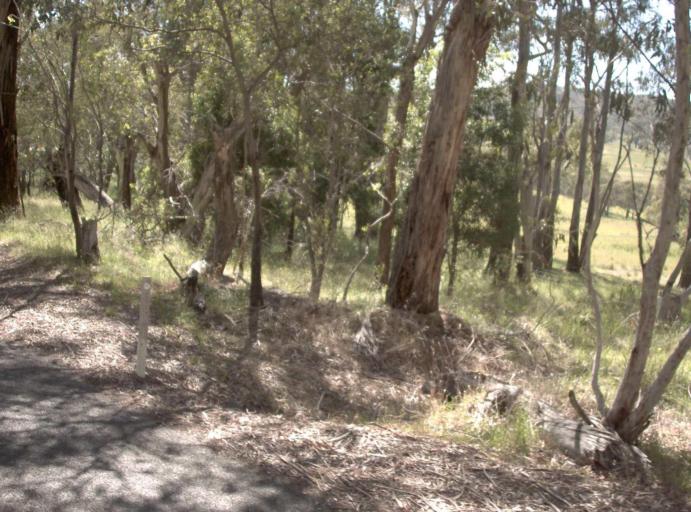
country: AU
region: New South Wales
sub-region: Bombala
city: Bombala
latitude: -37.0505
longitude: 148.8090
